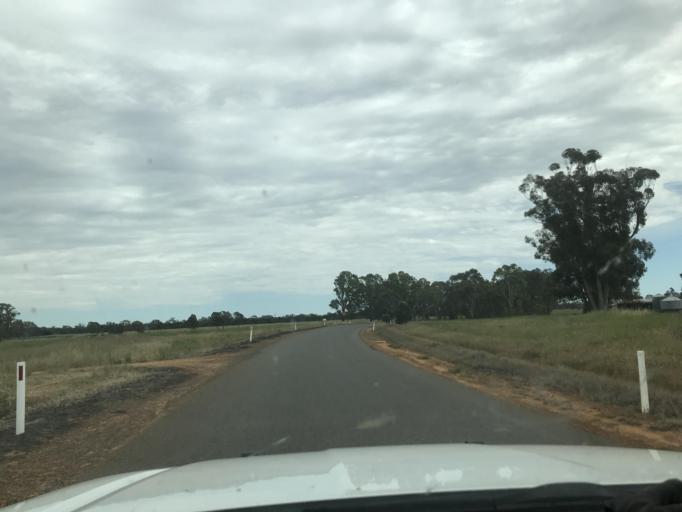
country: AU
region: Victoria
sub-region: Horsham
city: Horsham
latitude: -36.9768
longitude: 141.5241
